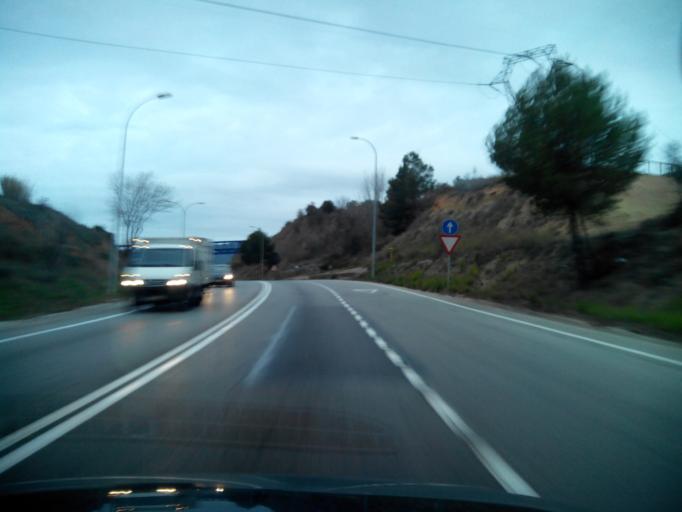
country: ES
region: Catalonia
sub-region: Provincia de Barcelona
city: Terrassa
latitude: 41.5563
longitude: 1.9866
